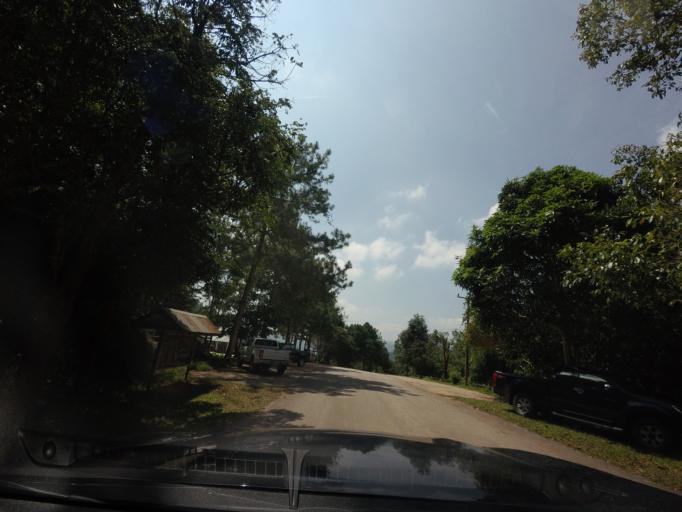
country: TH
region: Loei
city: Na Haeo
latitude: 17.5051
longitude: 100.9400
